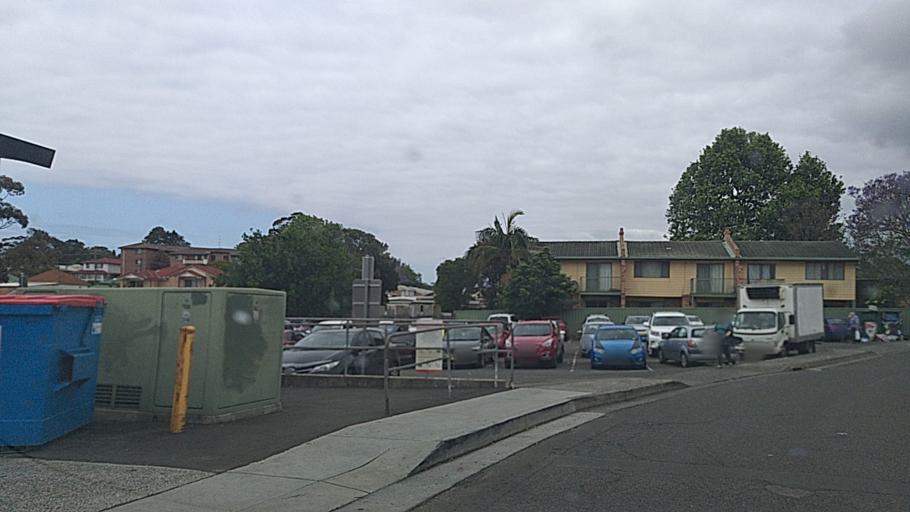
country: AU
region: New South Wales
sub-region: Wollongong
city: Bulli
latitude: -34.3415
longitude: 150.9073
